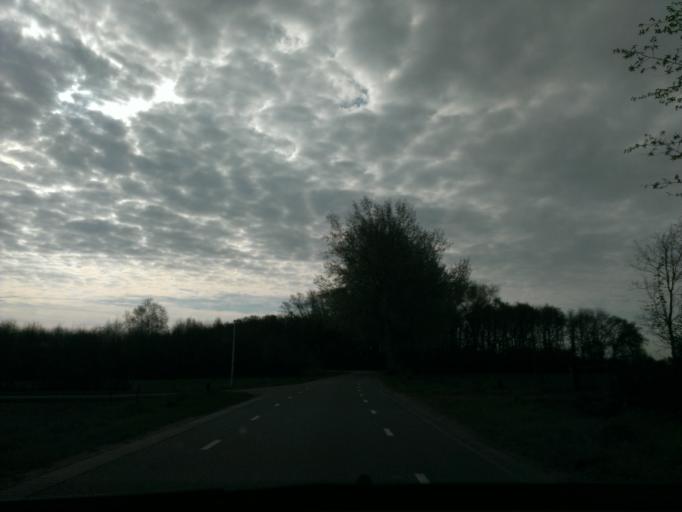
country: NL
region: Gelderland
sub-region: Gemeente Voorst
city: Twello
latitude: 52.2276
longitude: 6.0579
